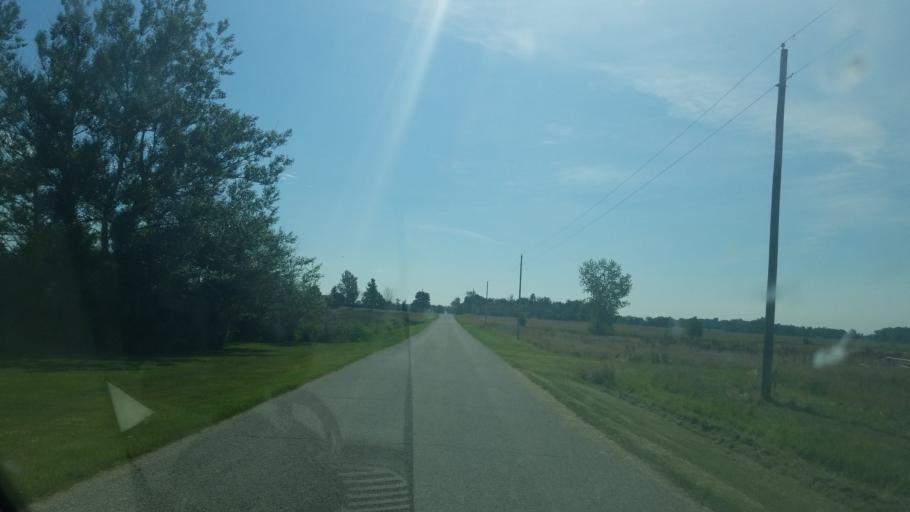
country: US
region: Ohio
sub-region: Wyandot County
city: Carey
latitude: 41.0142
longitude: -83.3309
